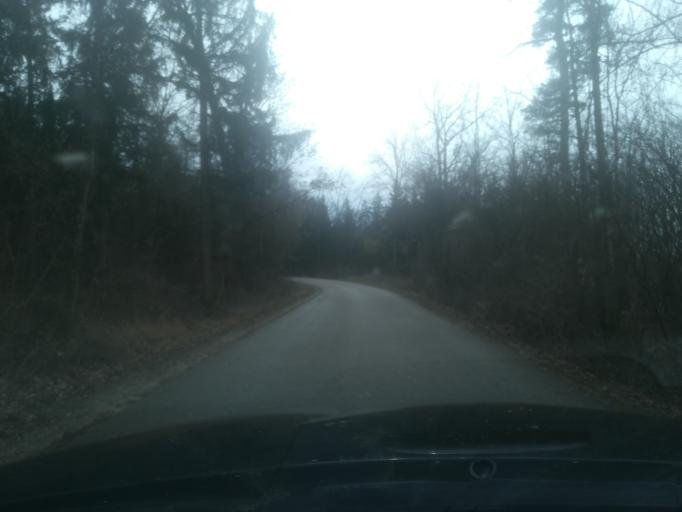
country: AT
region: Upper Austria
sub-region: Wels-Land
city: Gunskirchen
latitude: 48.1131
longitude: 13.9394
